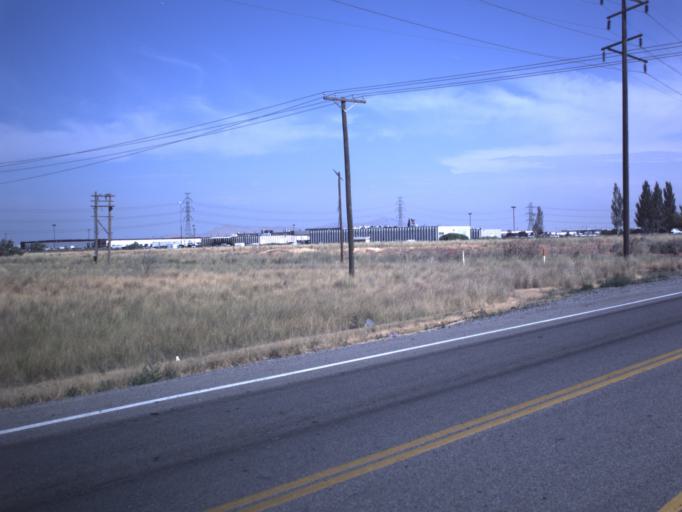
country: US
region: Utah
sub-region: Salt Lake County
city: West Valley City
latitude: 40.7493
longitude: -112.0249
